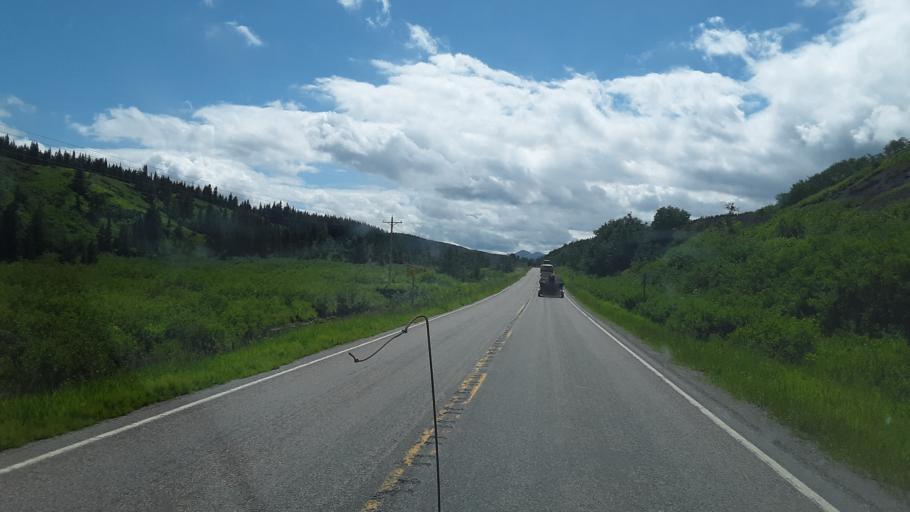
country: US
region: Montana
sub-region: Glacier County
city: South Browning
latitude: 48.3452
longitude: -113.3176
